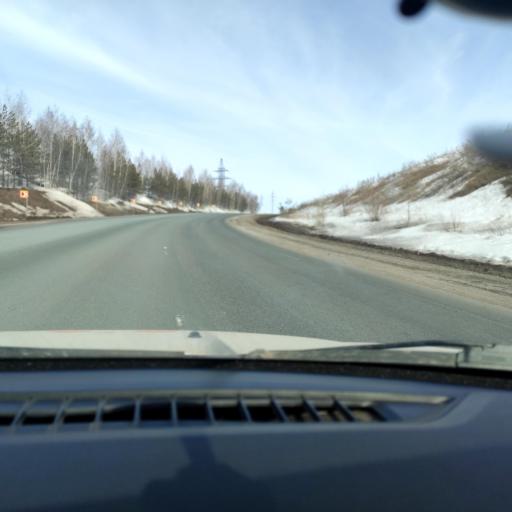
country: RU
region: Bashkortostan
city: Kushnarenkovo
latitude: 55.1645
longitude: 55.1251
